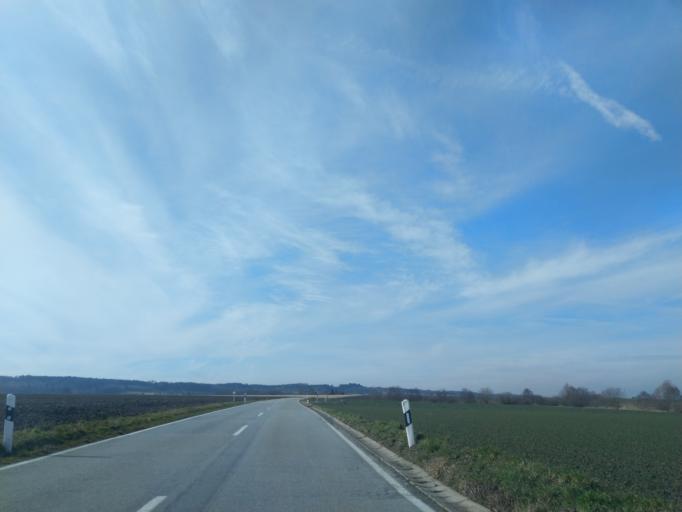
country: DE
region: Bavaria
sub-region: Lower Bavaria
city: Buchhofen
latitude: 48.6686
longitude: 12.9598
